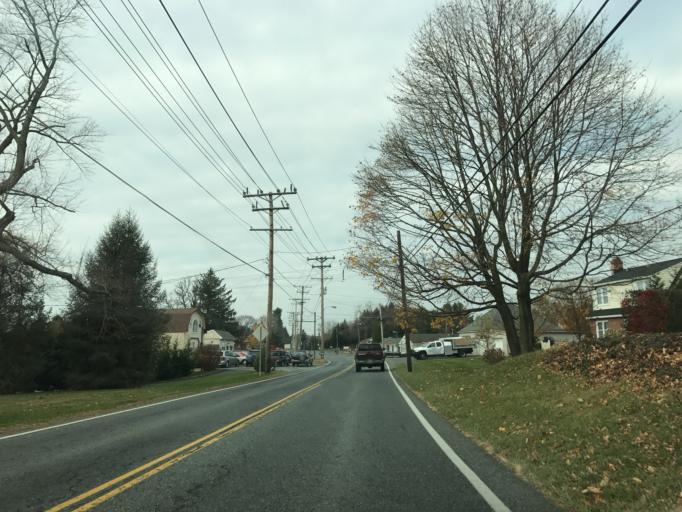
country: US
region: Maryland
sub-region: Harford County
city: Jarrettsville
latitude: 39.5915
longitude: -76.4333
